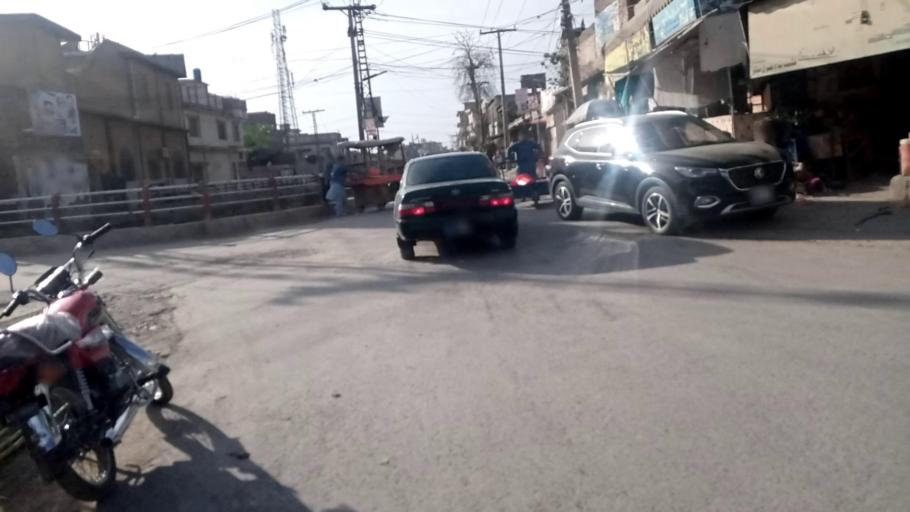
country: PK
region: Khyber Pakhtunkhwa
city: Peshawar
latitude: 34.0125
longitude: 71.6126
